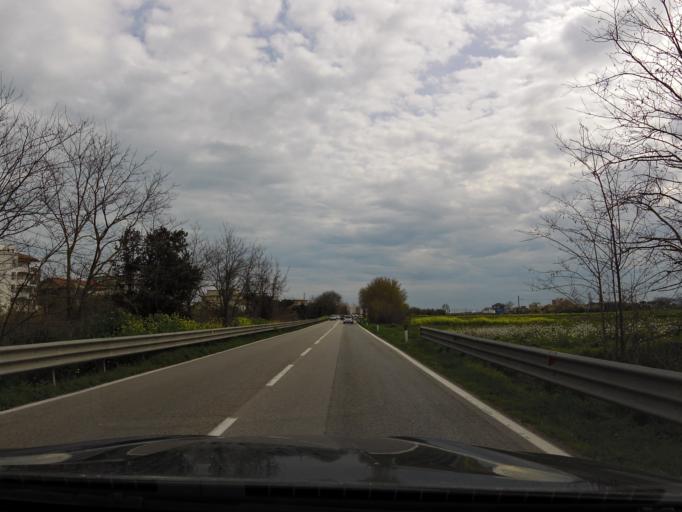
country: IT
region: The Marches
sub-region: Provincia di Macerata
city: Porto Recanati
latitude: 43.4140
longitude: 13.6721
